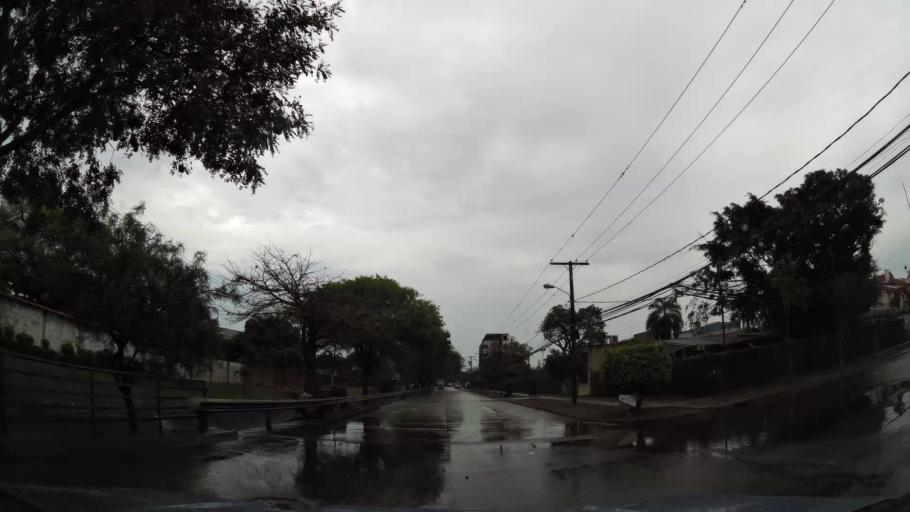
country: BO
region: Santa Cruz
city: Santa Cruz de la Sierra
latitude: -17.8032
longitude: -63.2019
